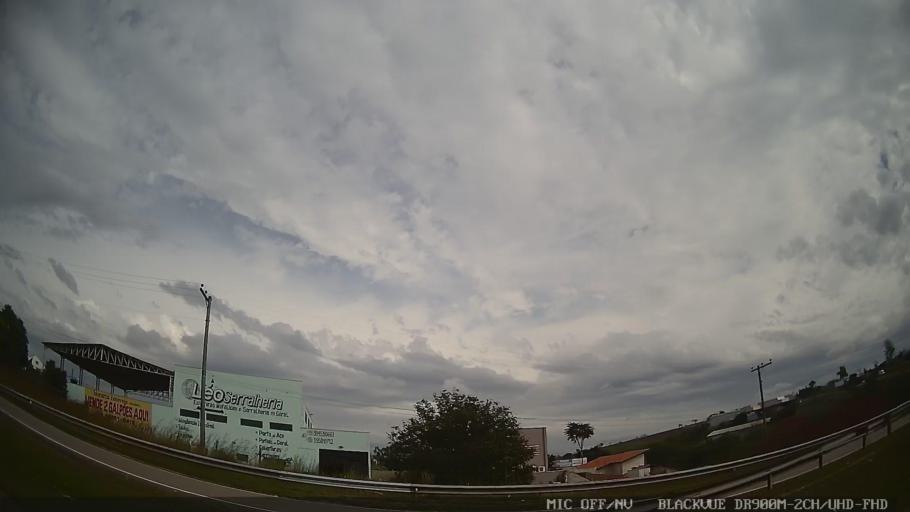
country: BR
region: Sao Paulo
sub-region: Salto
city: Salto
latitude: -23.1812
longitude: -47.2769
